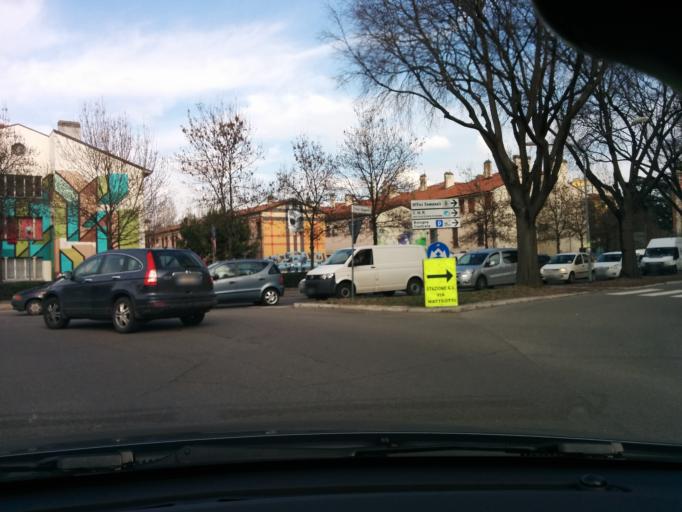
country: IT
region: Emilia-Romagna
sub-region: Provincia di Bologna
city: Bologna
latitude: 44.5172
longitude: 11.3286
